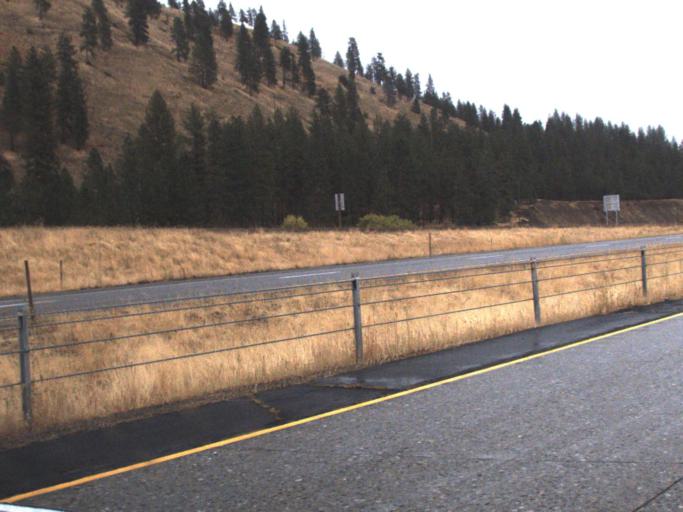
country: US
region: Washington
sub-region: Spokane County
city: Spokane
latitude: 47.6189
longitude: -117.4320
